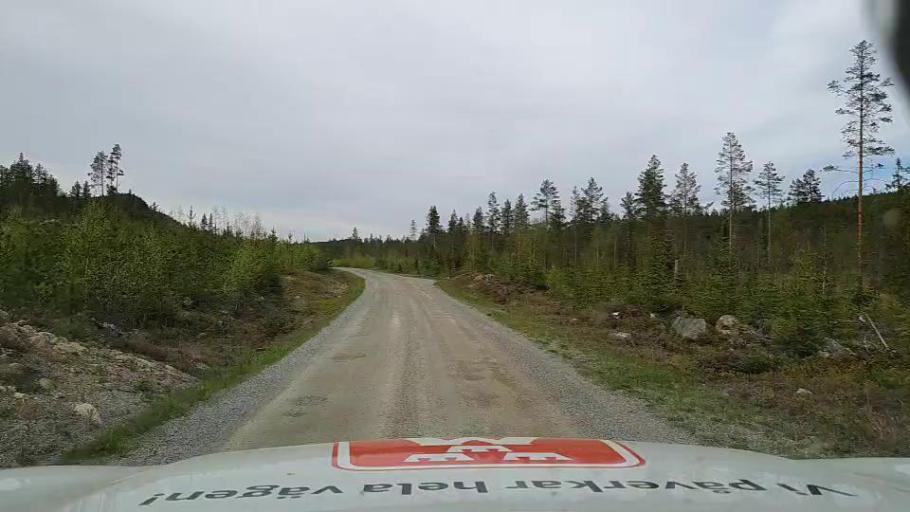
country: SE
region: Jaemtland
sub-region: Bergs Kommun
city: Hoverberg
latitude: 62.5495
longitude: 14.8981
